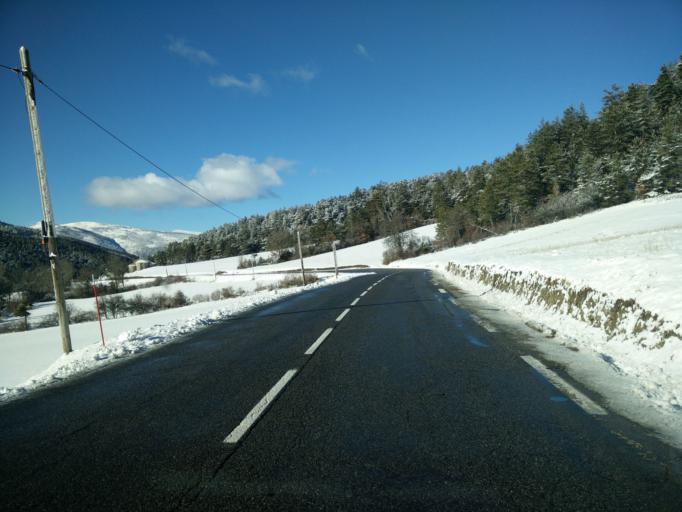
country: FR
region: Provence-Alpes-Cote d'Azur
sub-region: Departement des Alpes-de-Haute-Provence
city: Annot
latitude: 43.9127
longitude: 6.6001
